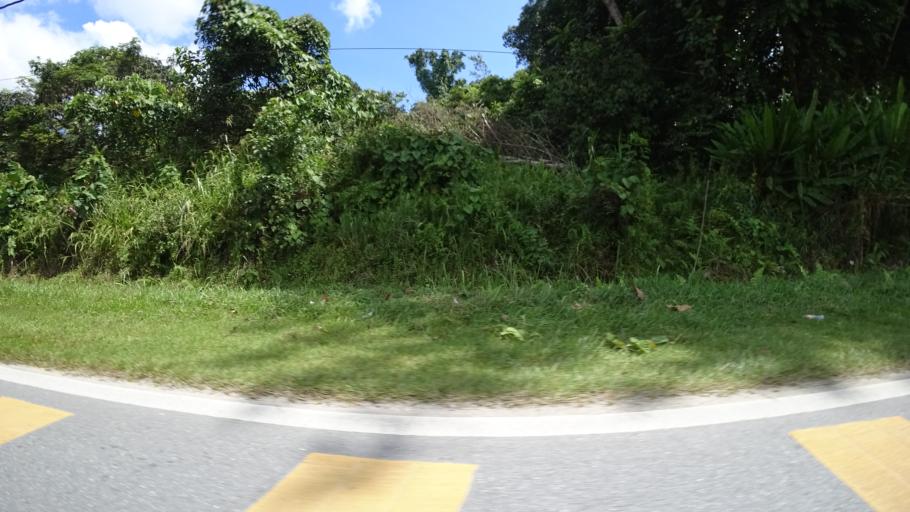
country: MY
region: Sarawak
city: Limbang
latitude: 4.6750
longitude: 114.9829
